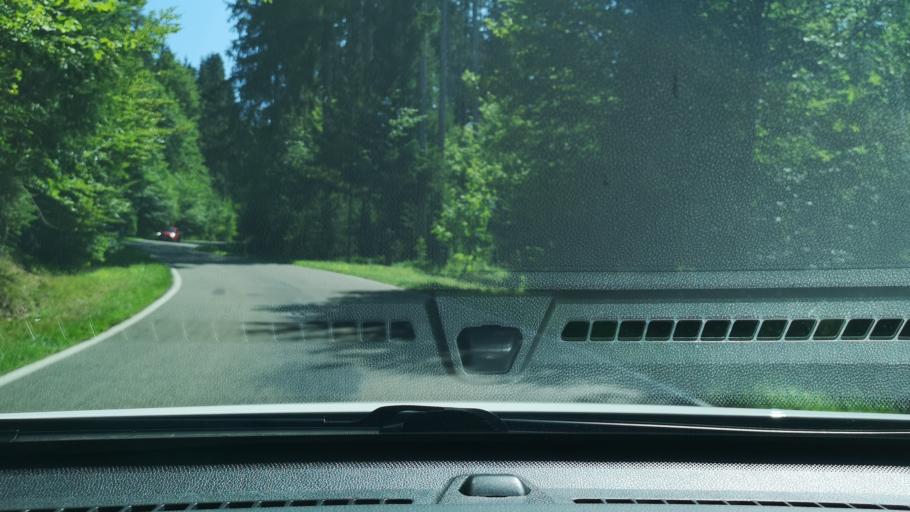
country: DE
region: Baden-Wuerttemberg
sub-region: Freiburg Region
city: Muhlheim am Bach
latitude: 48.3549
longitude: 8.7149
